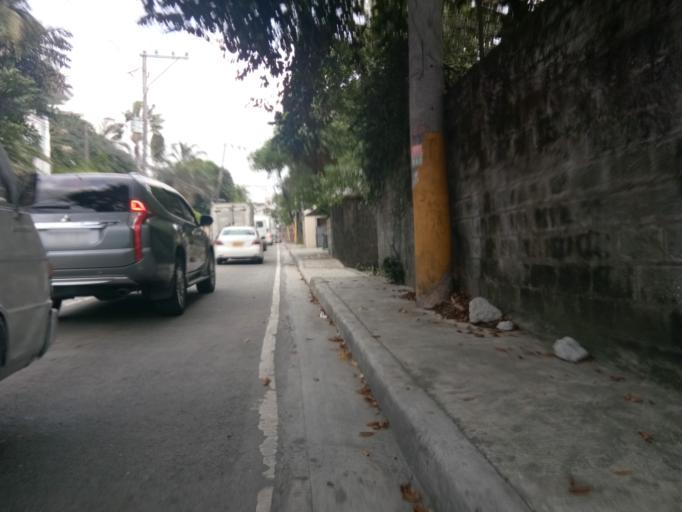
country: PH
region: Metro Manila
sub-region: San Juan
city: San Juan
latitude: 14.6116
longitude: 121.0452
